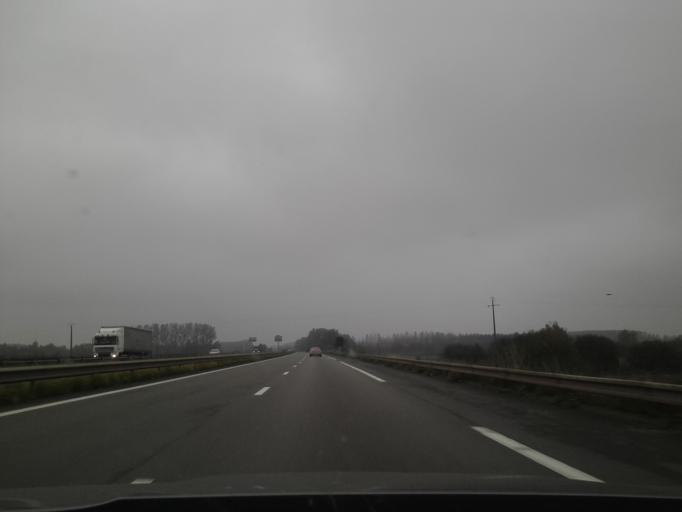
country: FR
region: Nord-Pas-de-Calais
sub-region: Departement du Nord
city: Crespin
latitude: 50.4349
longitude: 3.6580
